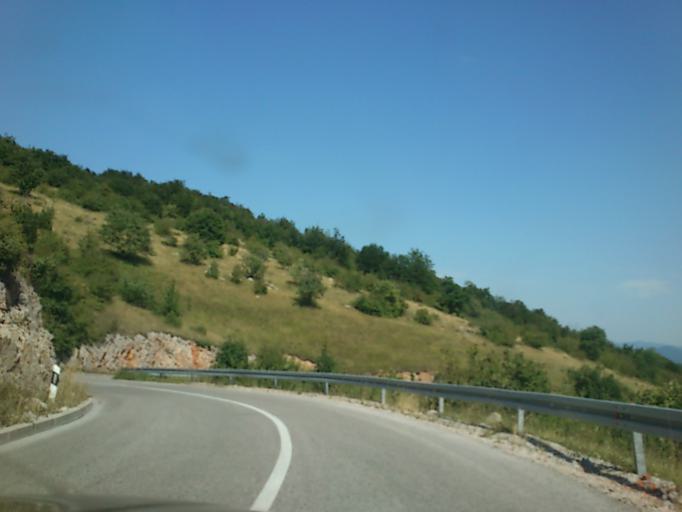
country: HR
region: Licko-Senjska
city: Otocac
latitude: 44.8297
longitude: 15.1113
